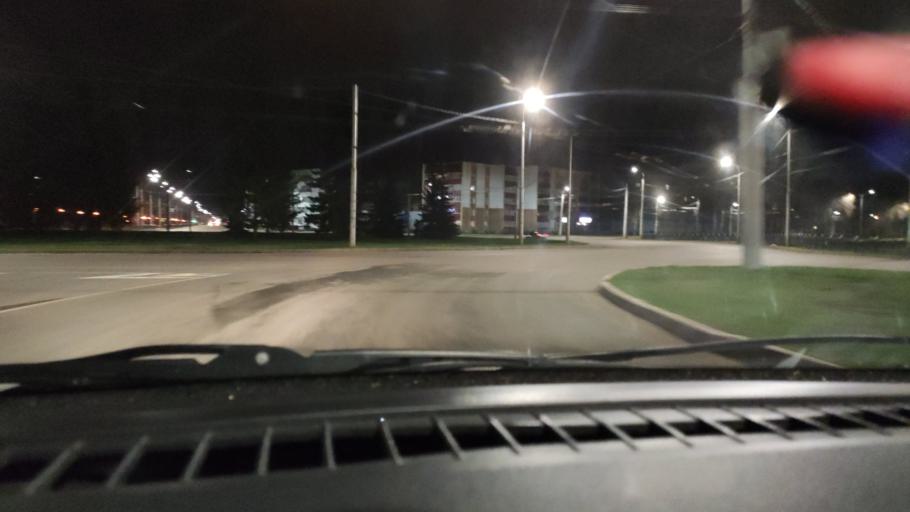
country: RU
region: Bashkortostan
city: Sterlitamak
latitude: 53.6381
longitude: 55.9088
